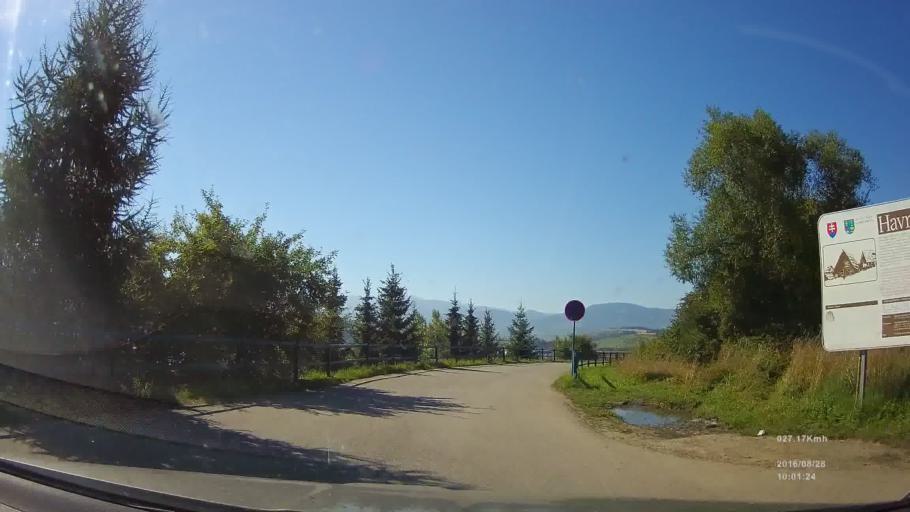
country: SK
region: Zilinsky
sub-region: Okres Liptovsky Mikulas
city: Liptovsky Mikulas
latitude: 49.1049
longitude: 19.4872
